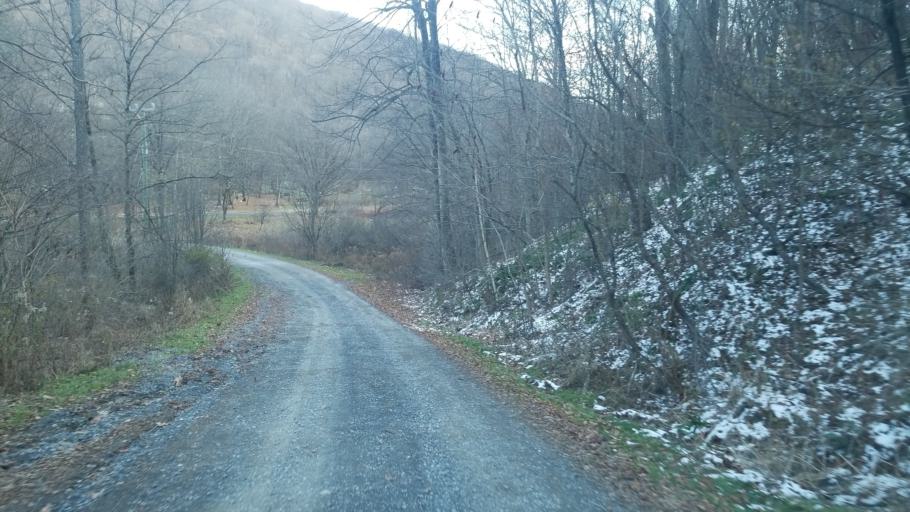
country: US
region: Pennsylvania
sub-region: Potter County
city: Coudersport
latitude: 41.6524
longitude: -78.0866
